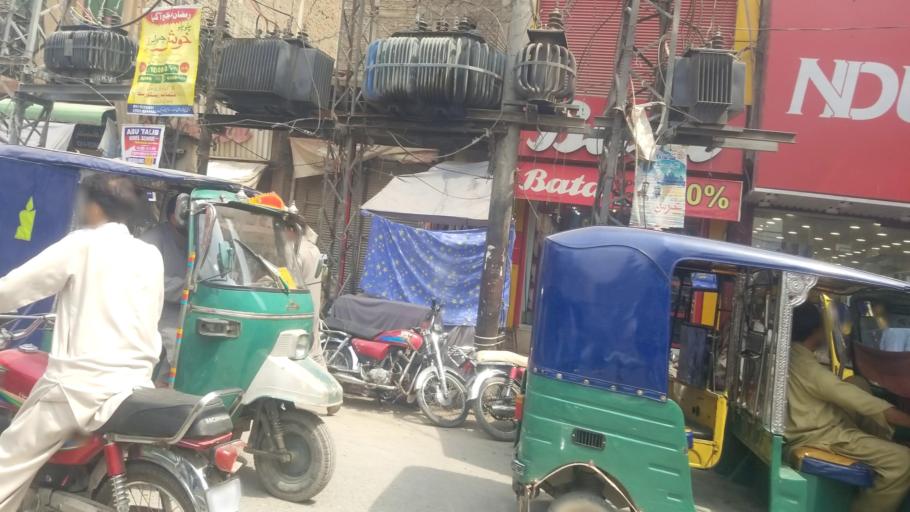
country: PK
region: Khyber Pakhtunkhwa
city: Peshawar
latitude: 34.0072
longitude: 71.5717
